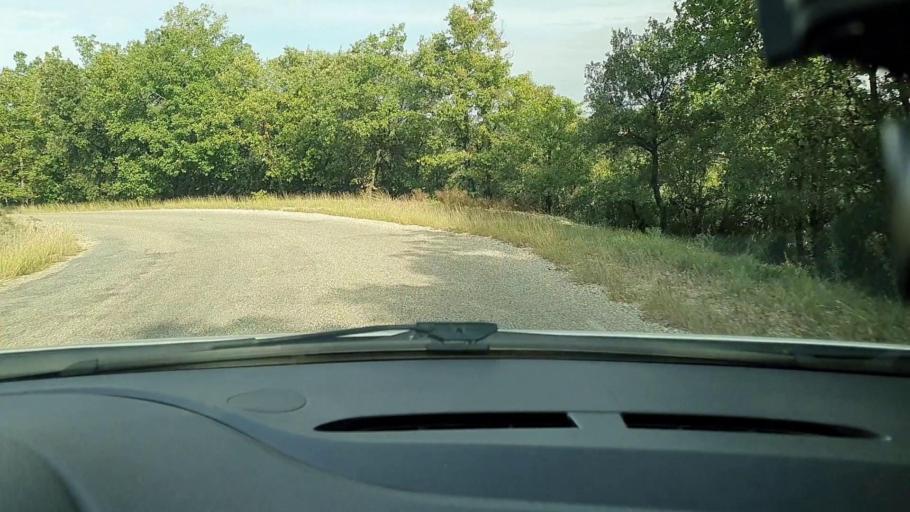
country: FR
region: Languedoc-Roussillon
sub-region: Departement du Gard
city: Saint-Quentin-la-Poterie
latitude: 44.1291
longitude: 4.4033
